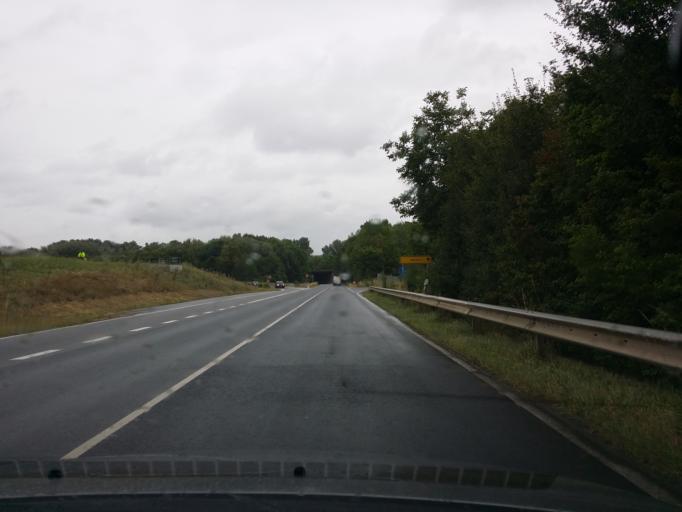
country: DE
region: Rheinland-Pfalz
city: Nackenheim
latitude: 49.9294
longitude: 8.3387
